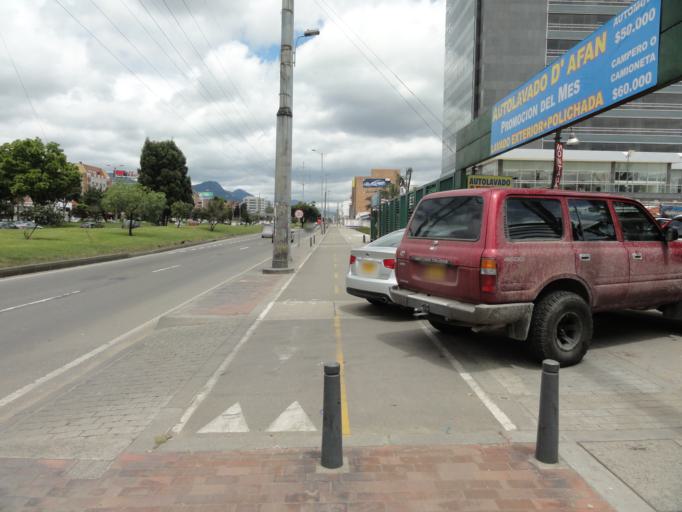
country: CO
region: Bogota D.C.
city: Barrio San Luis
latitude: 4.6970
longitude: -74.0560
